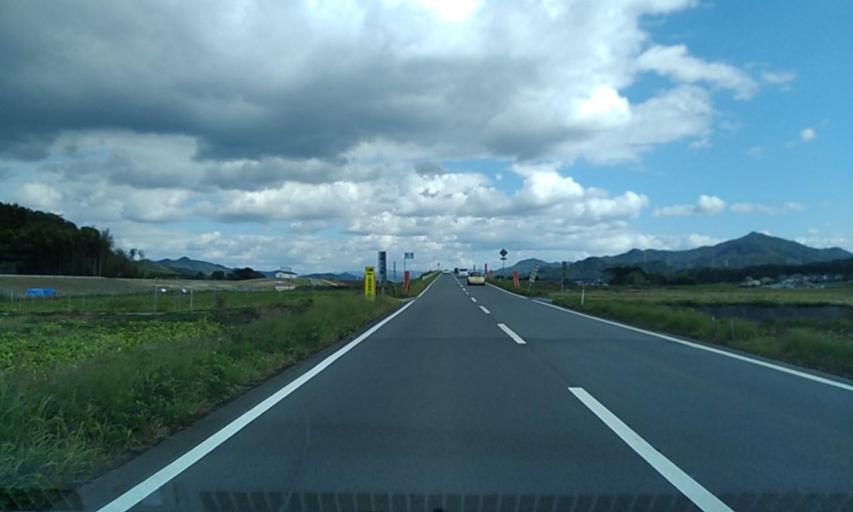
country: JP
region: Kyoto
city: Fukuchiyama
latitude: 35.3031
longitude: 135.1508
